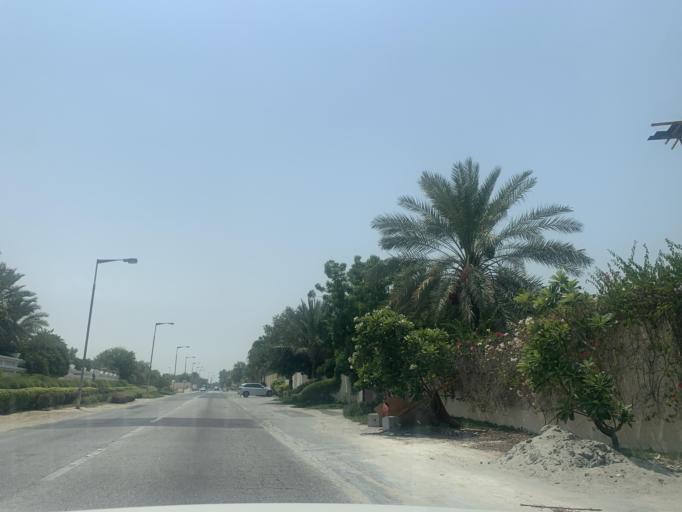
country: BH
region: Central Governorate
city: Madinat Hamad
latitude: 26.1518
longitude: 50.4642
